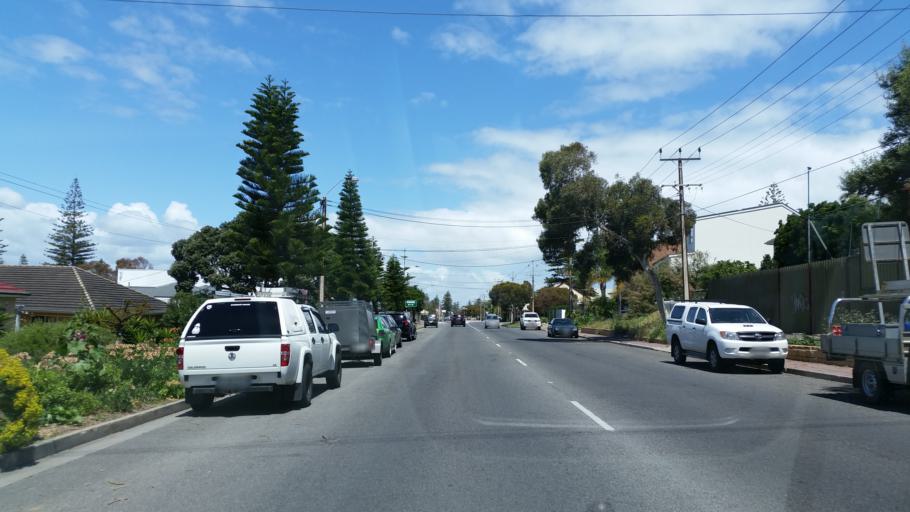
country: AU
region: South Australia
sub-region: Charles Sturt
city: Grange
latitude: -34.9036
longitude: 138.4911
